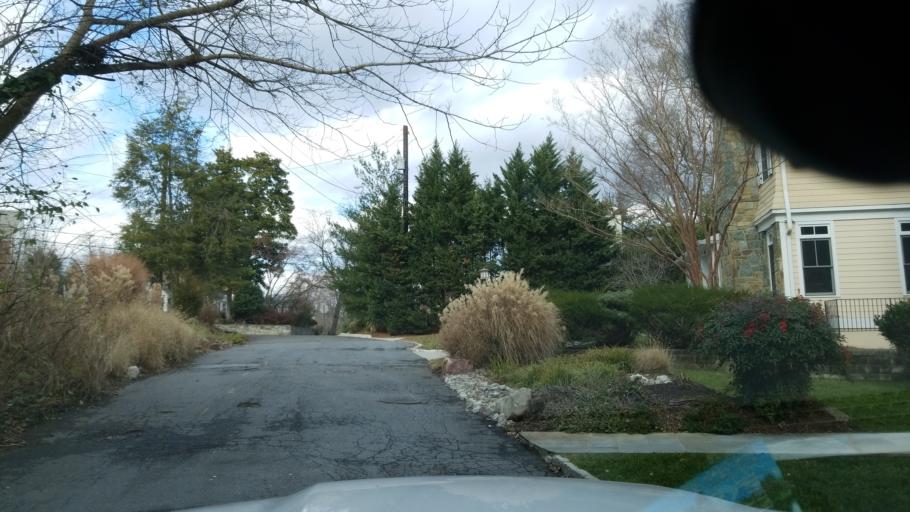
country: US
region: Maryland
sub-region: Montgomery County
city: Chevy Chase
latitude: 38.9666
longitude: -77.0567
